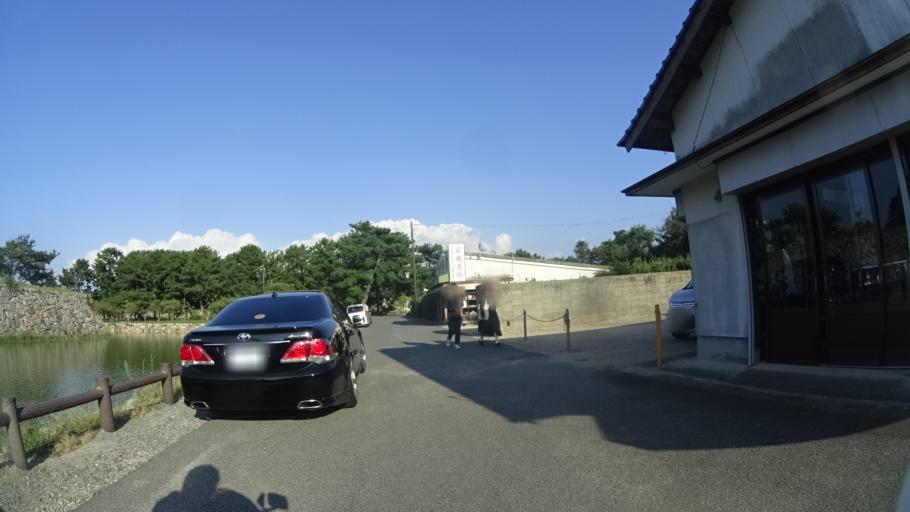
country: JP
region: Yamaguchi
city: Hagi
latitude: 34.4169
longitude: 131.3838
